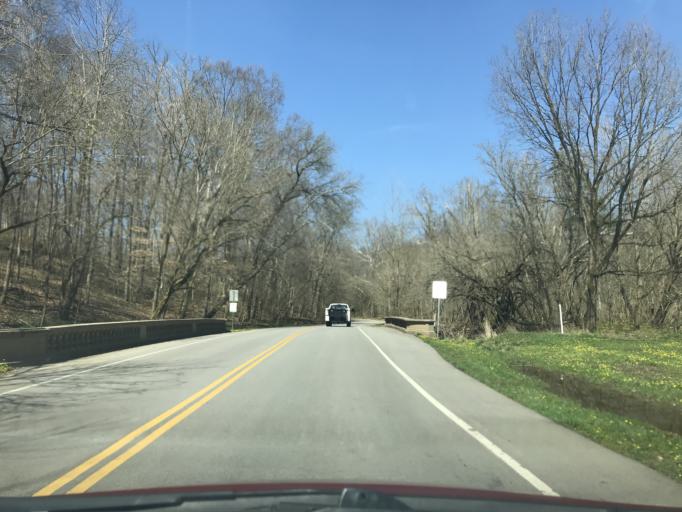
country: US
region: Kentucky
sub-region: Jefferson County
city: Saint Matthews
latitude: 38.2381
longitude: -85.6915
